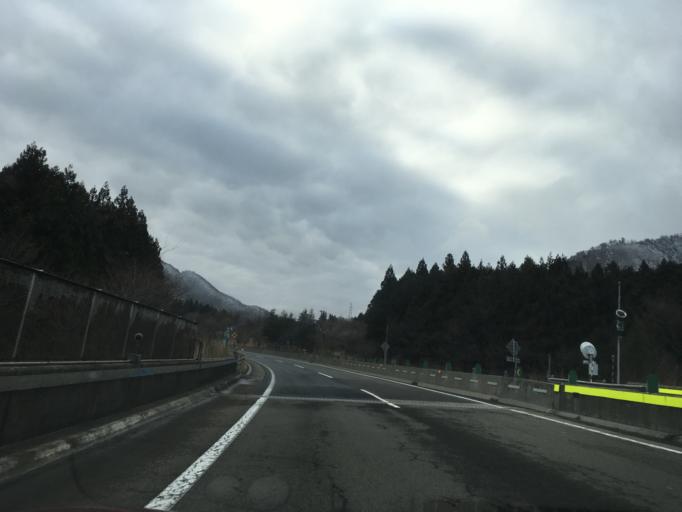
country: JP
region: Miyagi
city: Shiroishi
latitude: 38.2060
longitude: 140.5768
